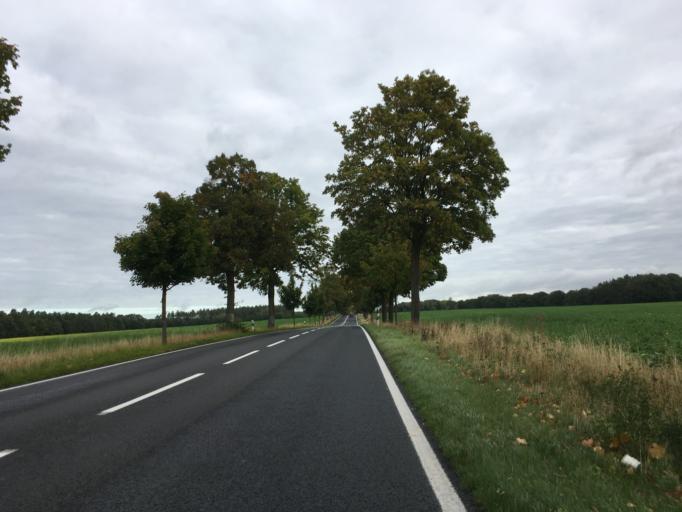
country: DE
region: Brandenburg
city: Werftpfuhl
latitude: 52.6942
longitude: 13.8650
